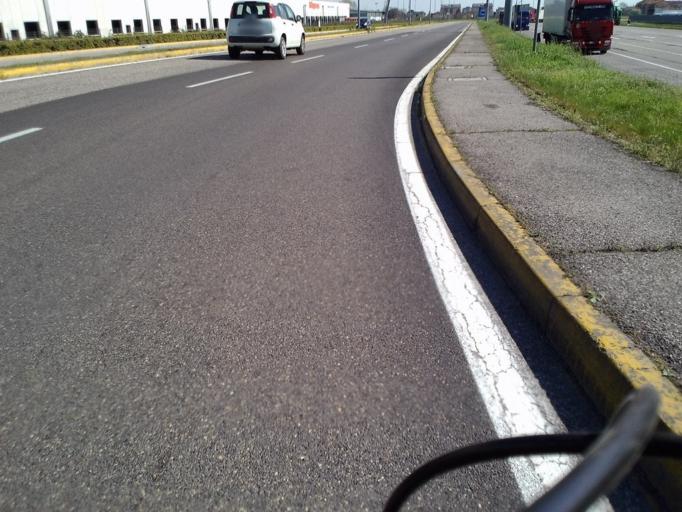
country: IT
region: Veneto
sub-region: Provincia di Verona
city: Dossobuono
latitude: 45.4130
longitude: 10.9253
